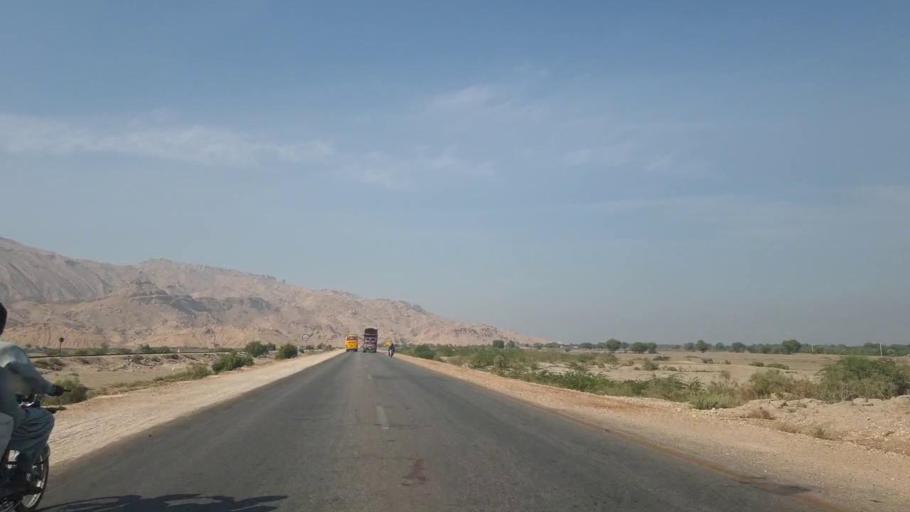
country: PK
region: Sindh
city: Sehwan
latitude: 26.2780
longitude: 67.8977
